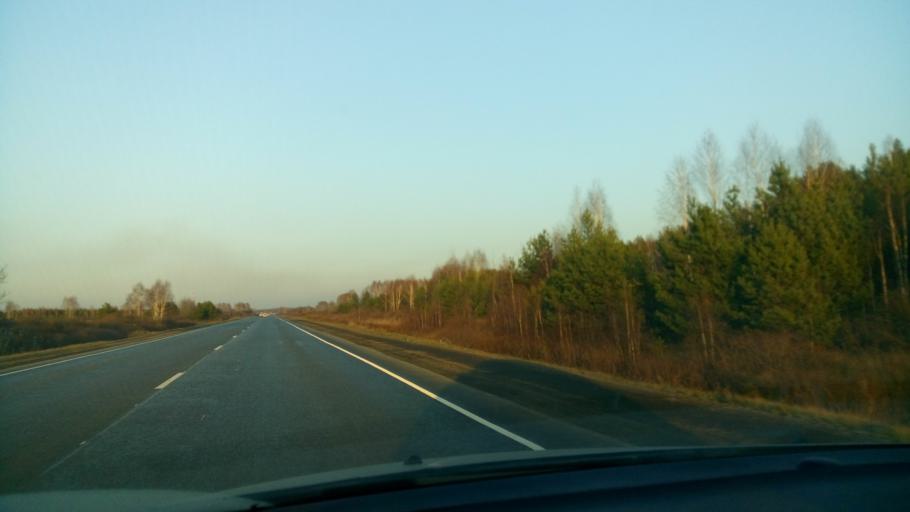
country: RU
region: Sverdlovsk
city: Obukhovskoye
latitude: 56.8271
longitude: 62.5589
